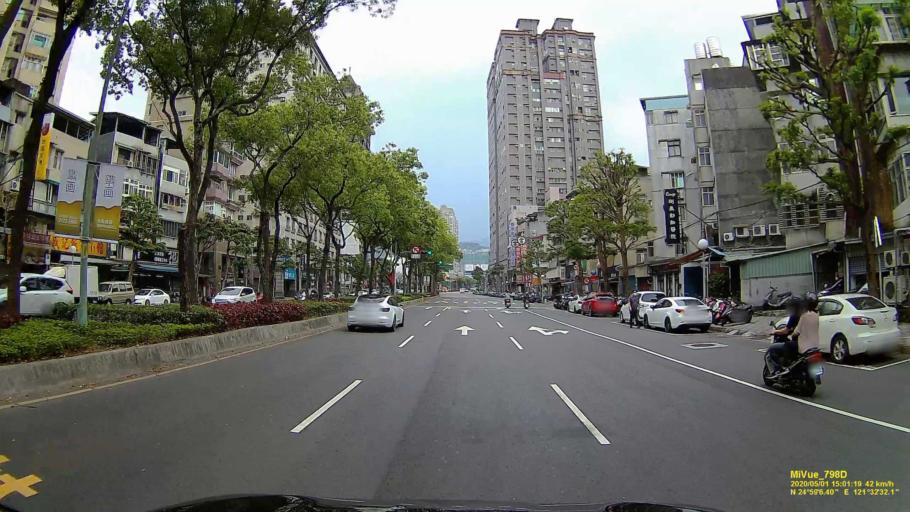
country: TW
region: Taipei
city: Taipei
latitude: 24.9849
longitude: 121.5423
